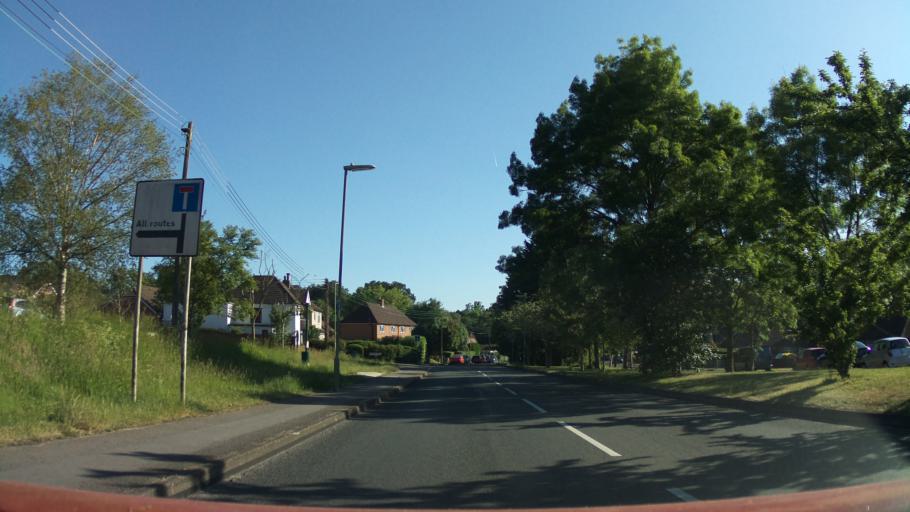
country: GB
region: England
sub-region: Hampshire
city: Compton
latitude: 50.9961
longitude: -1.3522
